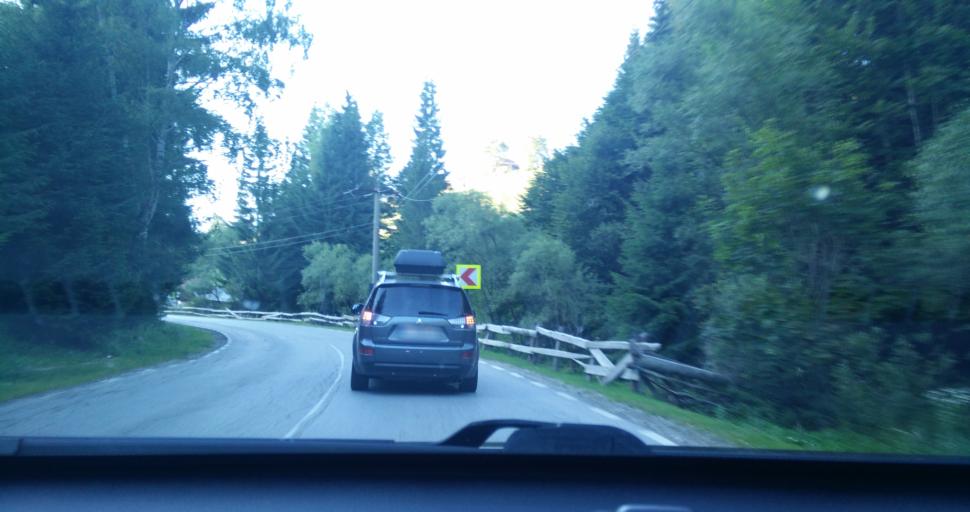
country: RO
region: Alba
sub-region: Comuna Arieseni
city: Arieseni
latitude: 46.4972
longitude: 22.7079
